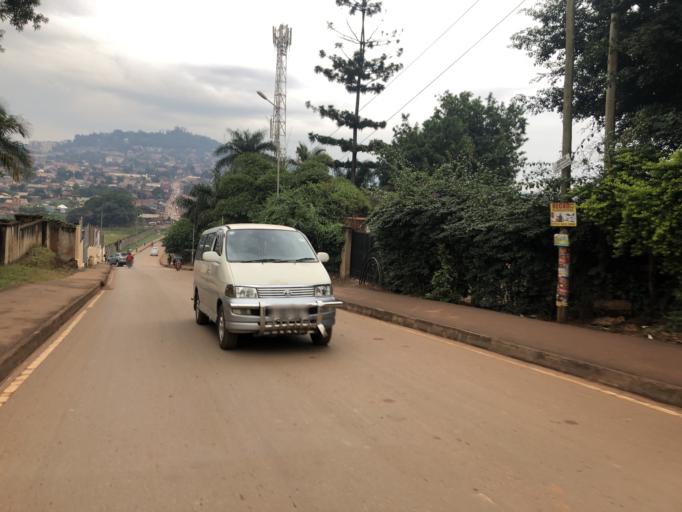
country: UG
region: Central Region
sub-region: Kampala District
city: Kampala
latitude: 0.2853
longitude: 32.6060
